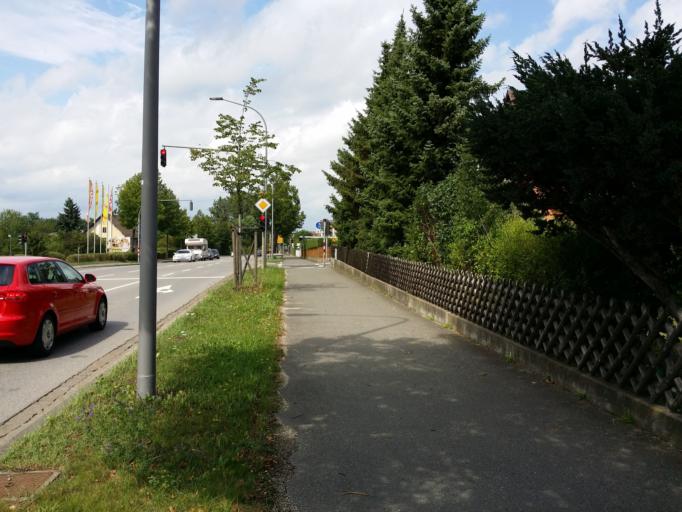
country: DE
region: Bavaria
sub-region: Upper Palatinate
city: Amberg
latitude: 49.4630
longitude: 11.8511
